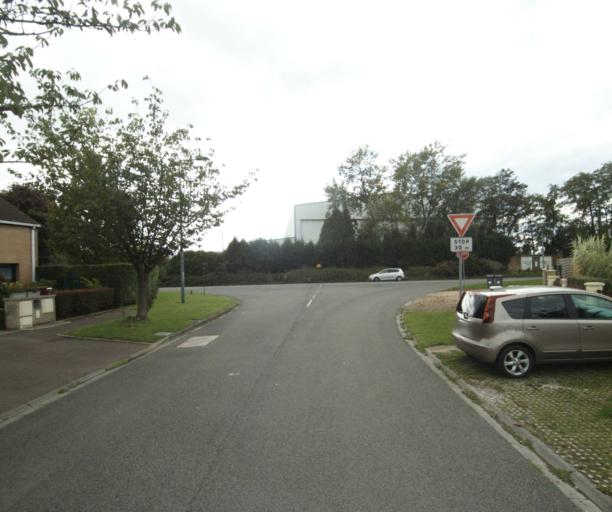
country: FR
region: Nord-Pas-de-Calais
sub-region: Departement du Nord
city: Lomme
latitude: 50.6390
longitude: 2.9825
